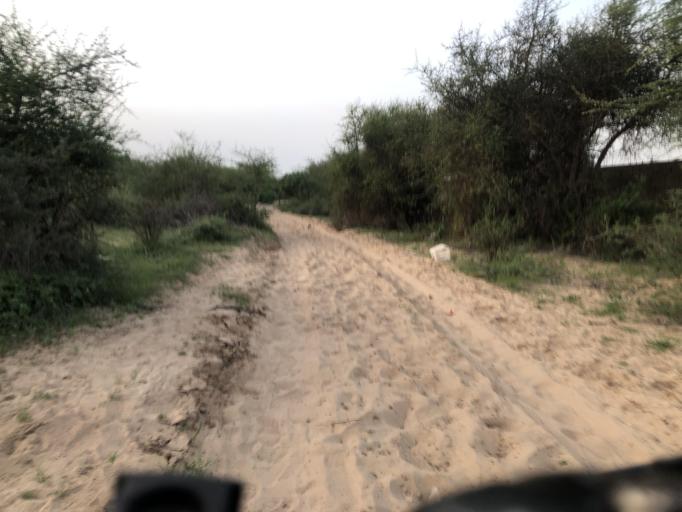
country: SN
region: Saint-Louis
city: Saint-Louis
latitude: 16.0575
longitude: -16.4318
